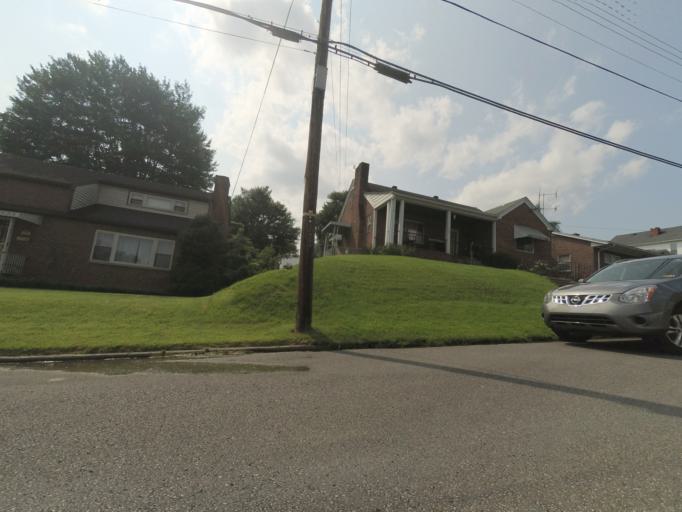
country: US
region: West Virginia
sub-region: Cabell County
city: Huntington
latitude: 38.4035
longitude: -82.4021
